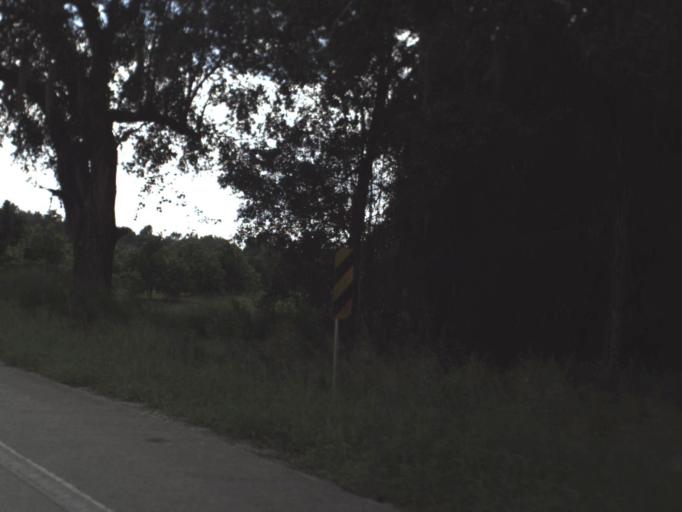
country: US
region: Florida
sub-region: Hardee County
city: Zolfo Springs
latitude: 27.5283
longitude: -81.7472
